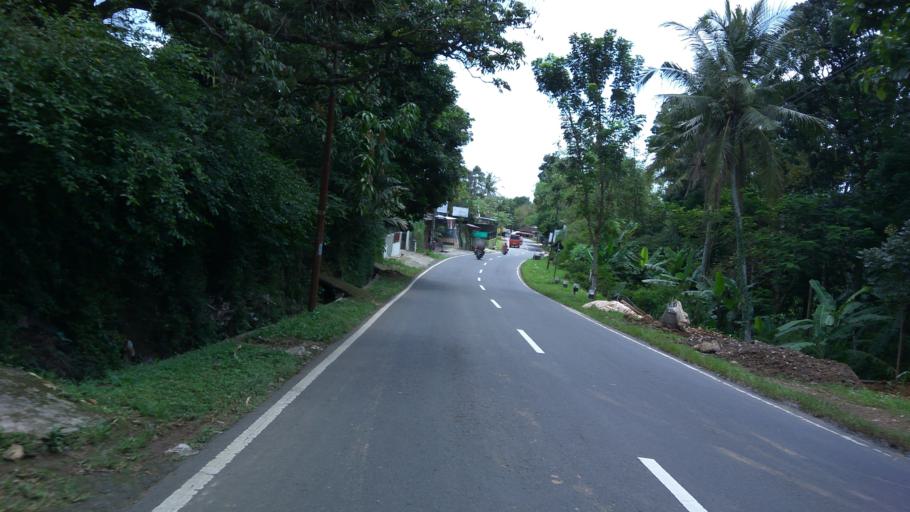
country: ID
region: Central Java
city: Ambarawa
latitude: -7.2423
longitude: 110.3920
